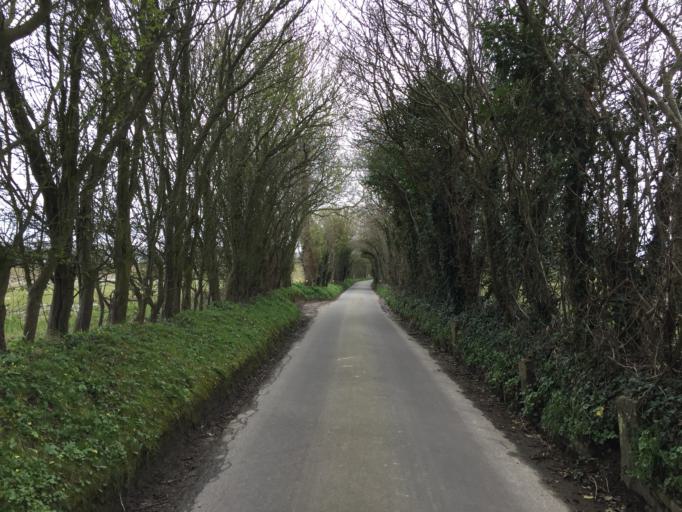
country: JE
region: St Helier
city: Saint Helier
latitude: 49.2038
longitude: -2.0621
